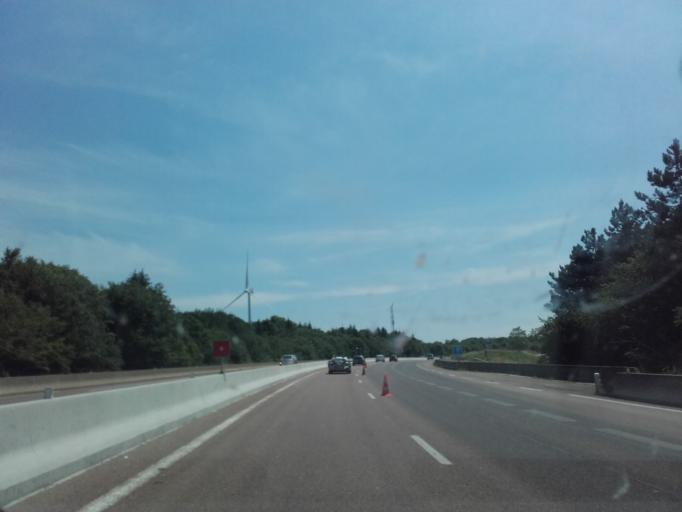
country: FR
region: Bourgogne
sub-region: Departement de la Cote-d'Or
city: Savigny-les-Beaune
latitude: 47.1024
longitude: 4.7367
